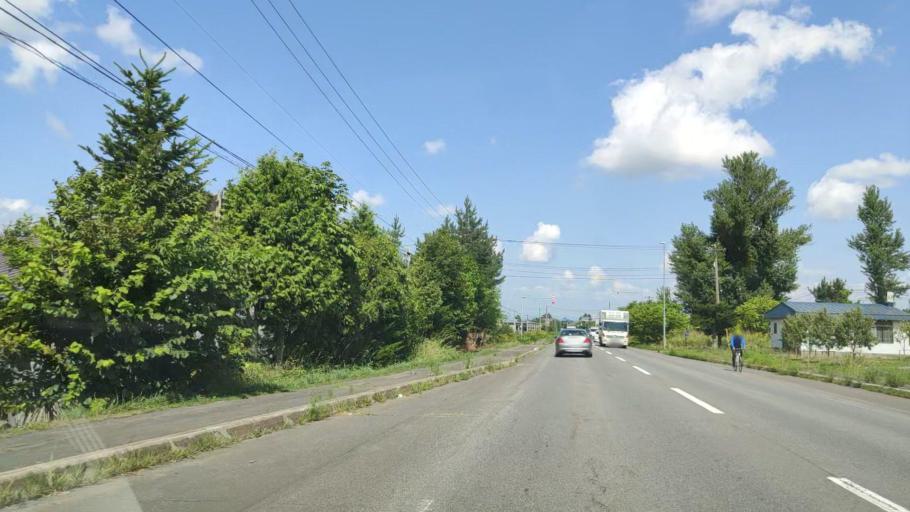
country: JP
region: Hokkaido
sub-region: Asahikawa-shi
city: Asahikawa
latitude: 43.6360
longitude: 142.4558
